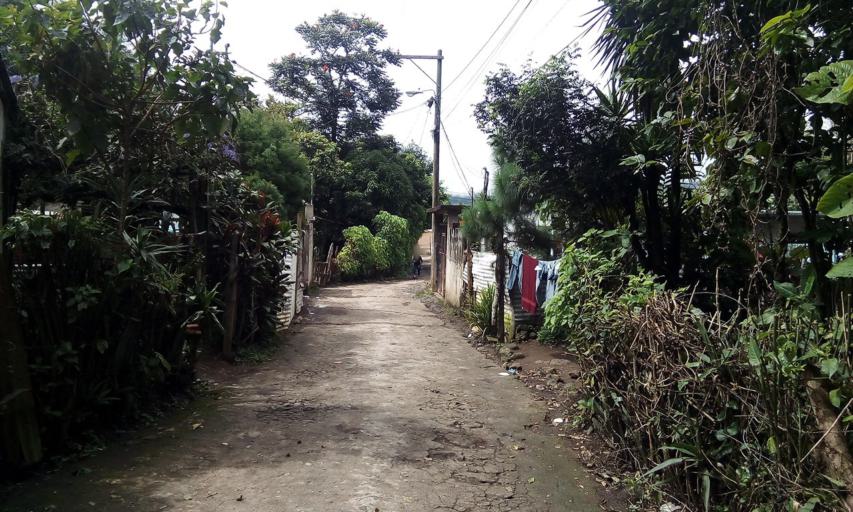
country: GT
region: Escuintla
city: San Vicente Pacaya
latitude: 14.3327
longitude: -90.6030
